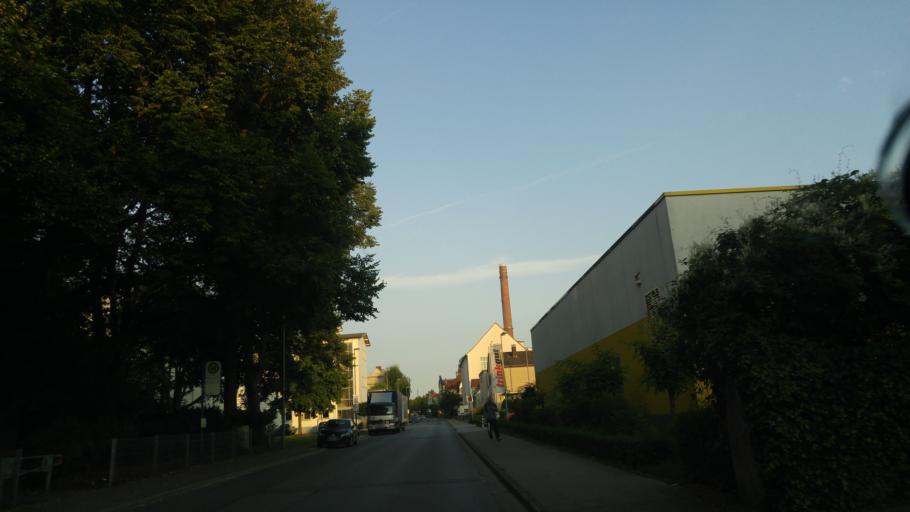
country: DE
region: North Rhine-Westphalia
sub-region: Regierungsbezirk Detmold
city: Bielefeld
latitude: 52.0377
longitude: 8.5342
